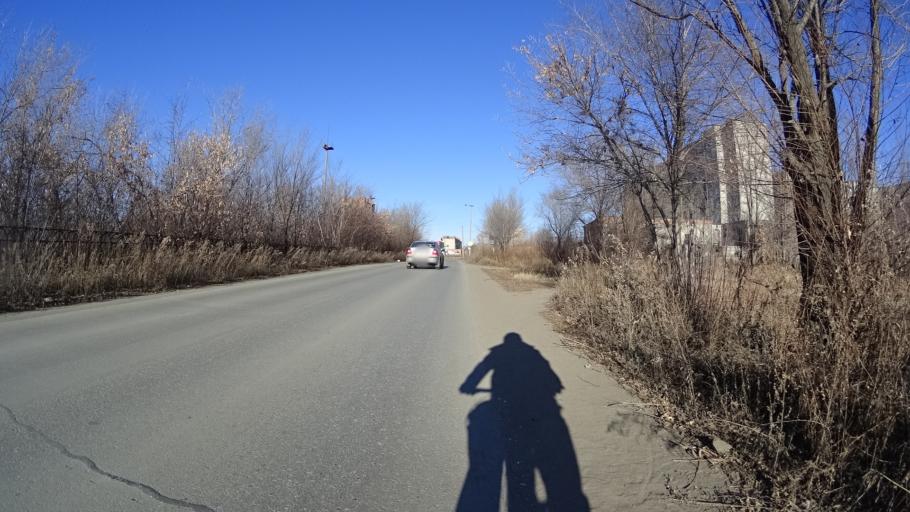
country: RU
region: Chelyabinsk
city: Troitsk
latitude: 54.0459
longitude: 61.6402
